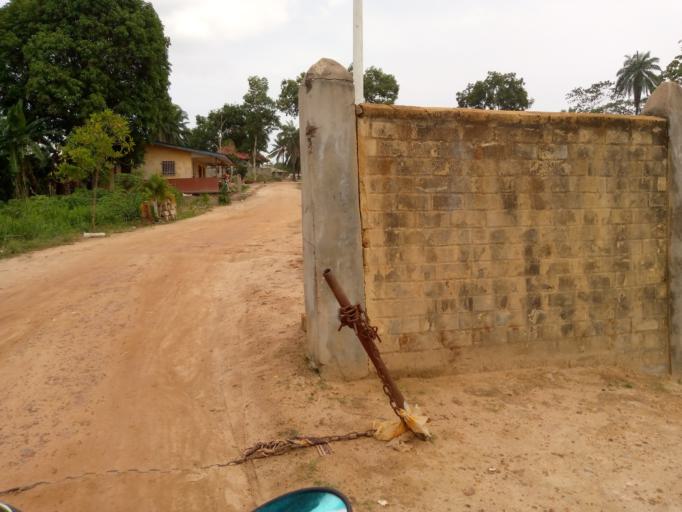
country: SL
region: Western Area
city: Waterloo
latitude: 8.3406
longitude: -13.0160
